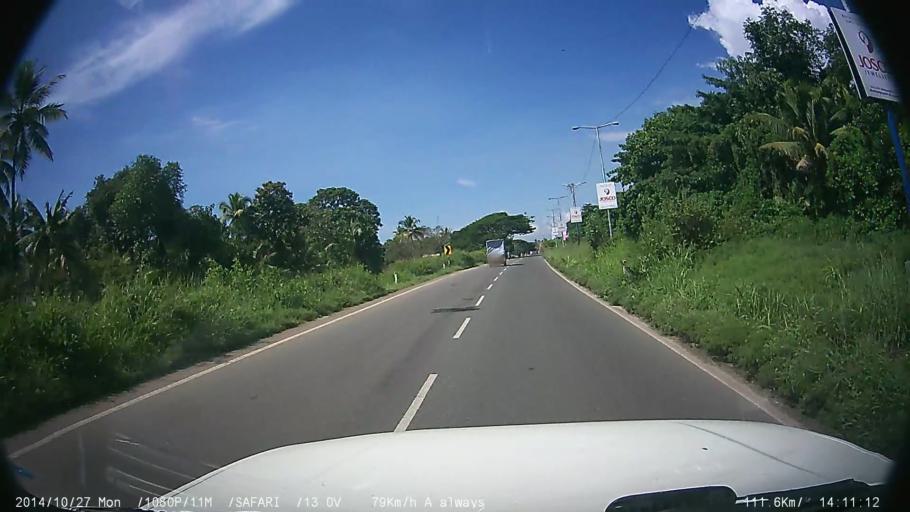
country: IN
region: Kerala
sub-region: Alappuzha
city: Kutiatodu
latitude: 9.7906
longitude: 76.3166
